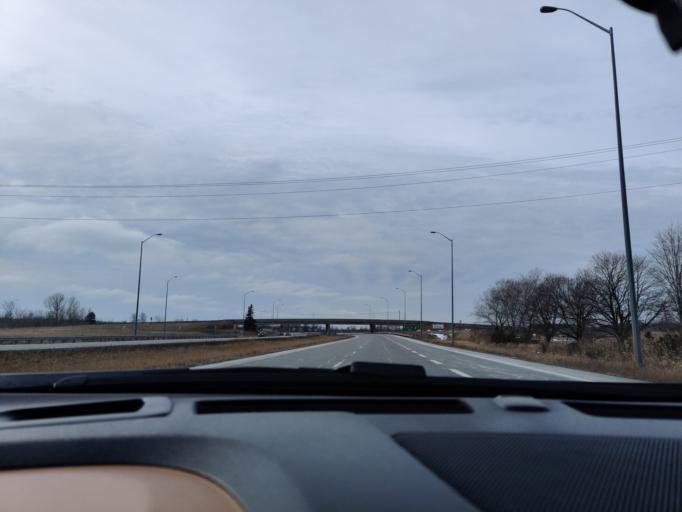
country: CA
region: Quebec
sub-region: Monteregie
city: Les Coteaux
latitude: 45.1940
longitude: -74.3785
